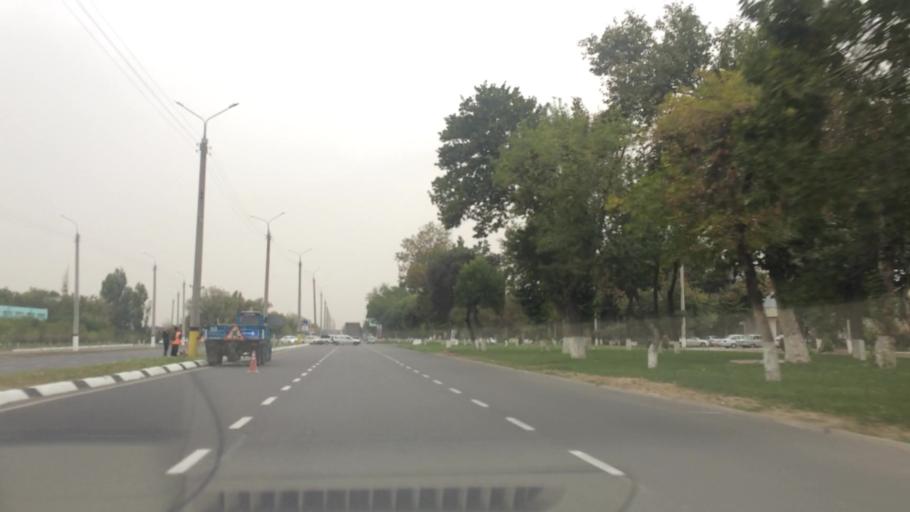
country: UZ
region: Toshkent
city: Salor
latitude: 41.3135
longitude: 69.3502
